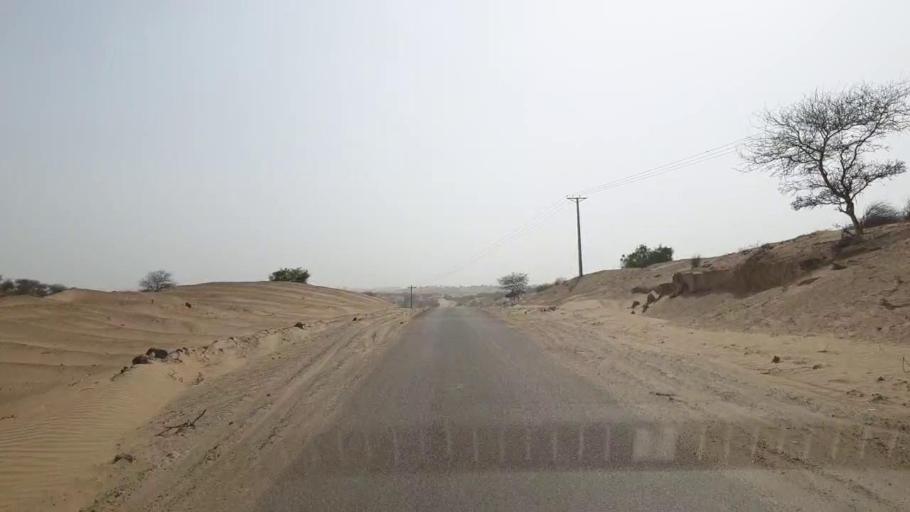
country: PK
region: Sindh
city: Mithi
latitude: 24.6205
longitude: 69.8968
